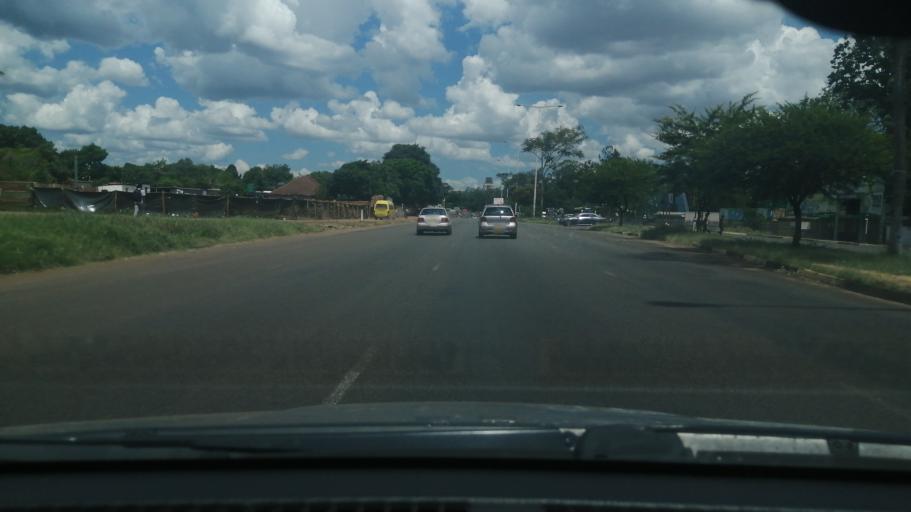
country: ZW
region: Harare
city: Harare
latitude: -17.8289
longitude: 31.0265
